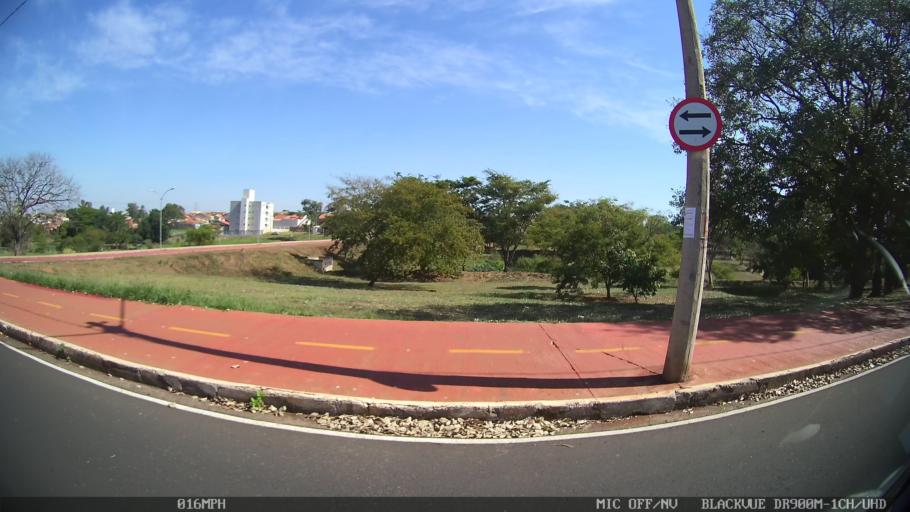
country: BR
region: Sao Paulo
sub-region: Sao Jose Do Rio Preto
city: Sao Jose do Rio Preto
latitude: -20.7847
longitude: -49.4144
